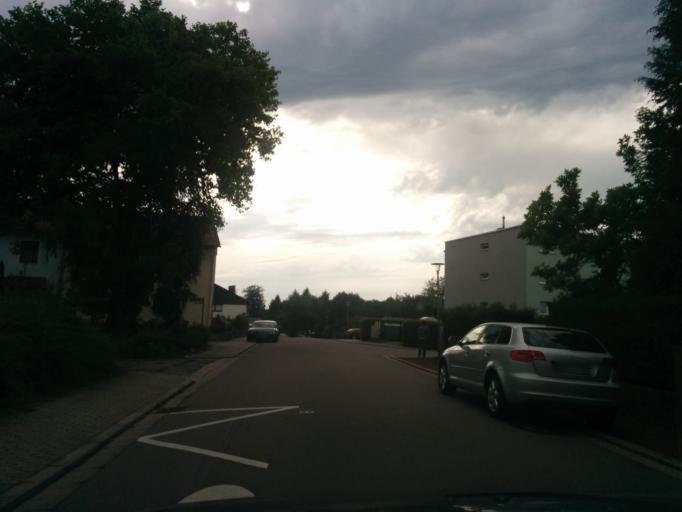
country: DE
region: Saarland
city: Sankt Ingbert
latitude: 49.2827
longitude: 7.0919
